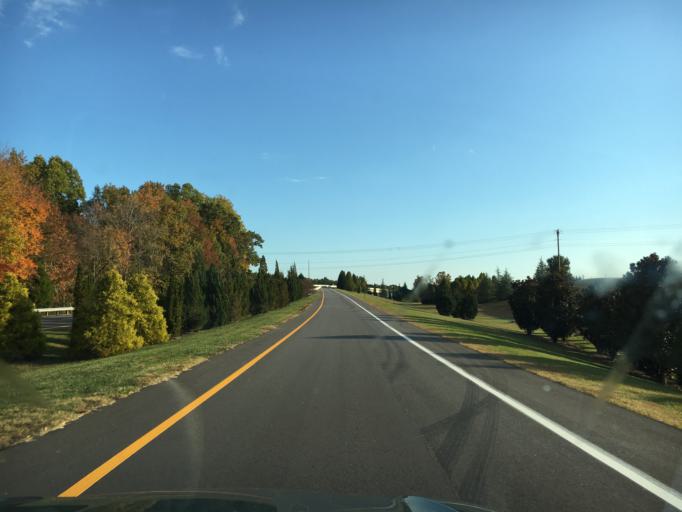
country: US
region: South Carolina
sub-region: Greenville County
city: Greer
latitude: 34.8806
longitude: -82.2149
